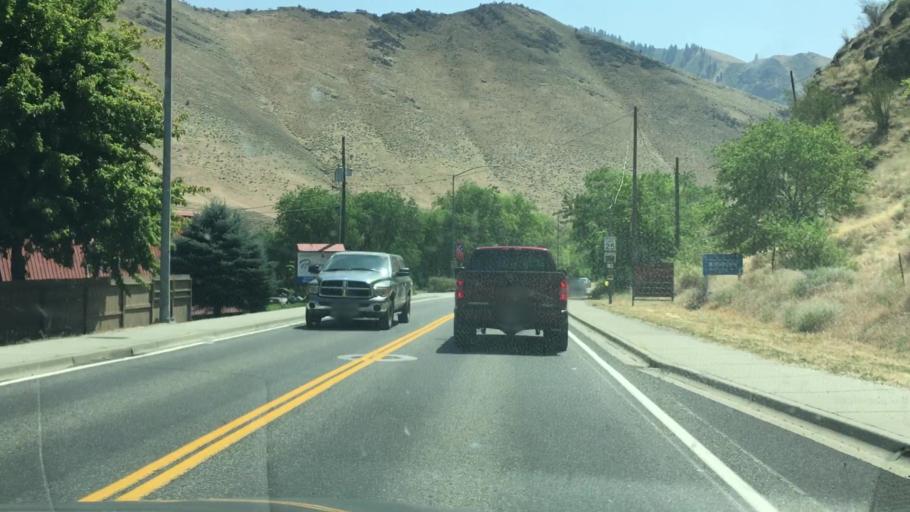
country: US
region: Idaho
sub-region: Idaho County
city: Grangeville
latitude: 45.4291
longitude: -116.3124
